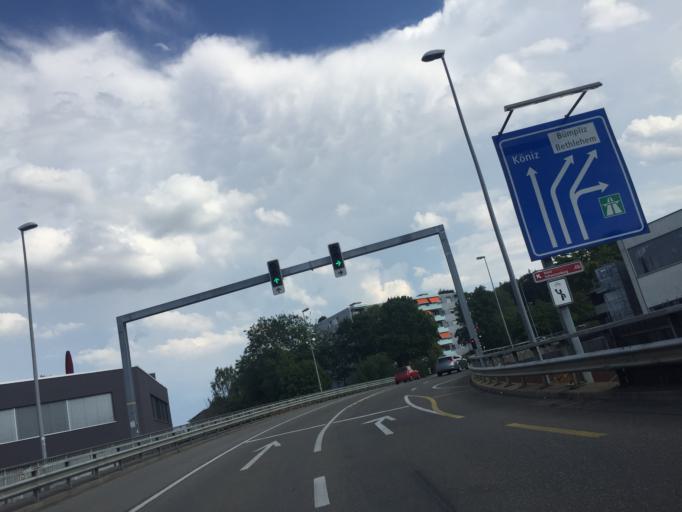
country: CH
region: Bern
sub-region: Bern-Mittelland District
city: Koniz
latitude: 46.9430
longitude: 7.4083
